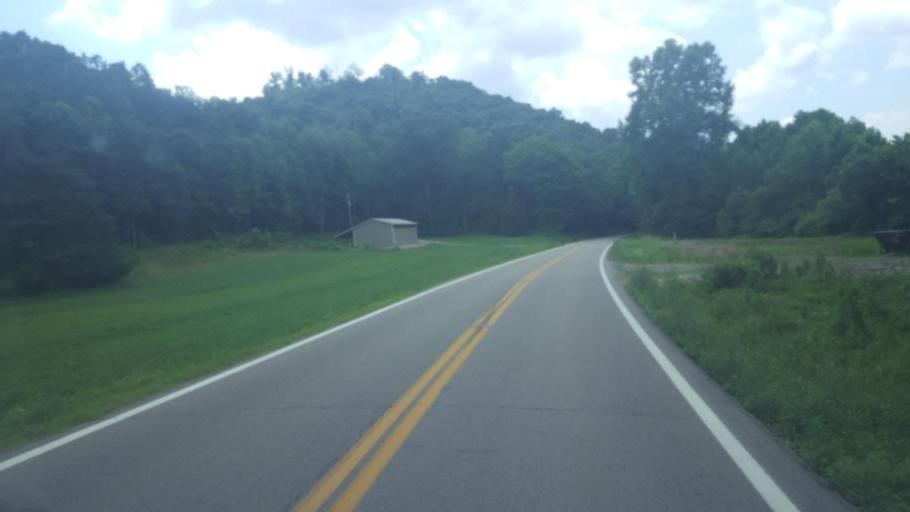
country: US
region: Ohio
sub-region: Ross County
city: Kingston
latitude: 39.3938
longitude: -82.7244
